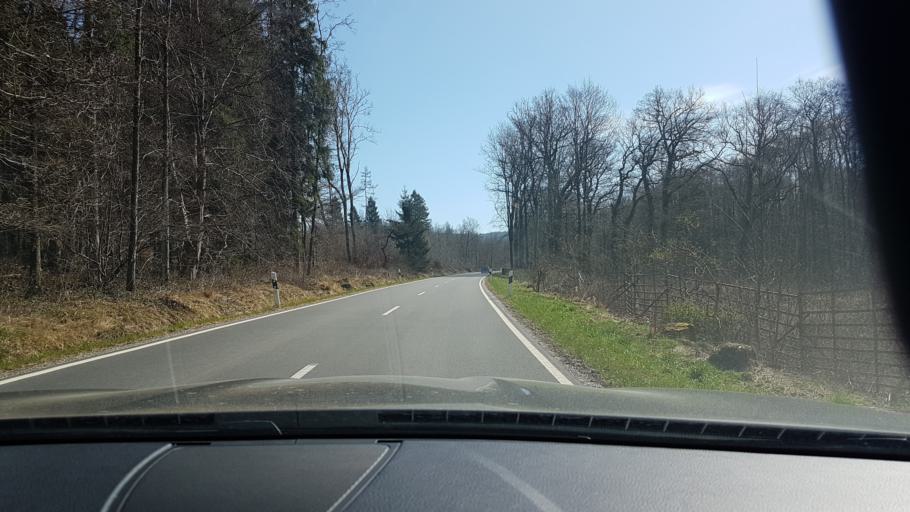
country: DE
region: Lower Saxony
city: Coppenbrugge
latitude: 52.1449
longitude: 9.5852
